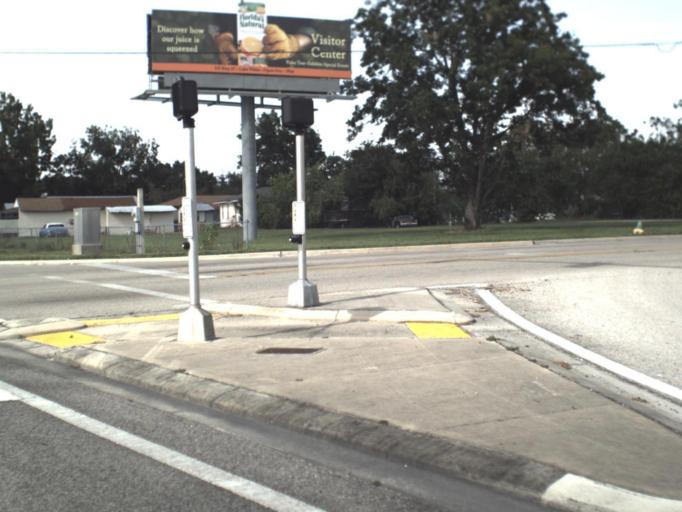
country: US
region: Florida
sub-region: Polk County
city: Lake Wales
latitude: 27.9133
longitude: -81.6031
